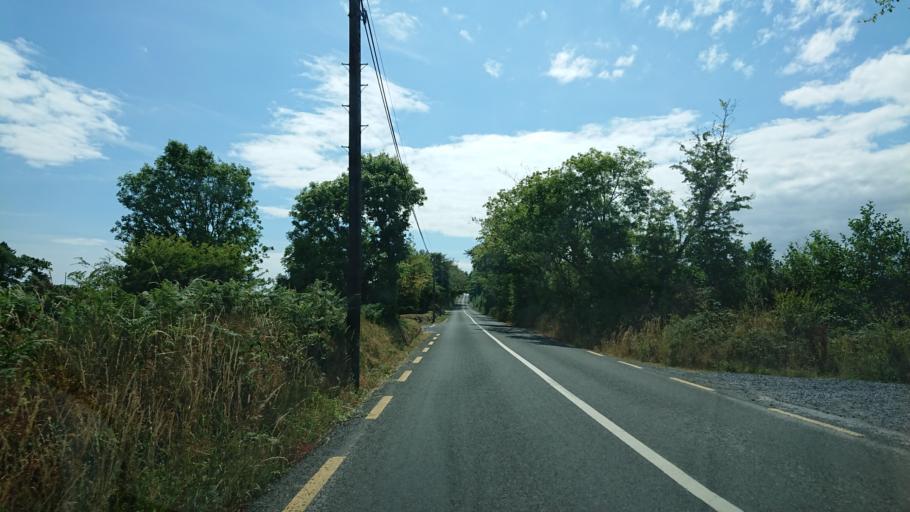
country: IE
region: Munster
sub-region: Waterford
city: Portlaw
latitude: 52.1651
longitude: -7.3387
